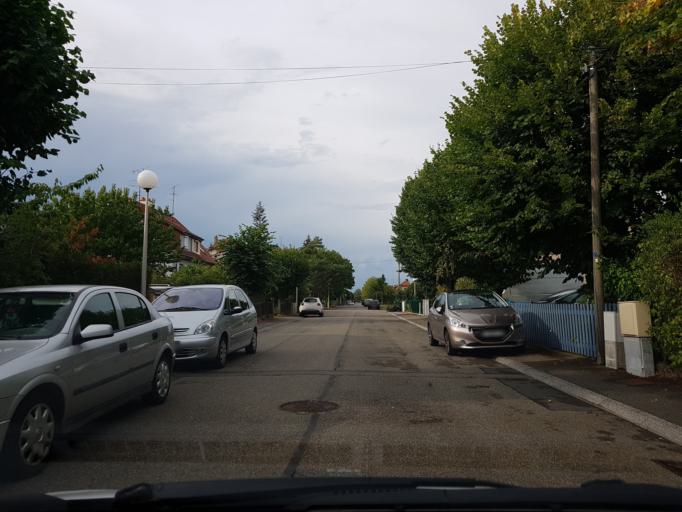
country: FR
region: Alsace
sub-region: Departement du Haut-Rhin
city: Wittenheim
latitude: 47.8242
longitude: 7.3373
